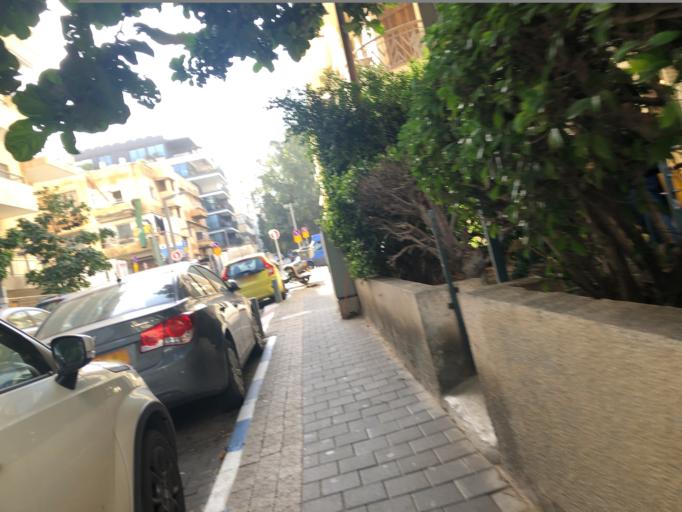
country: IL
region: Tel Aviv
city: Tel Aviv
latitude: 32.0691
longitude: 34.7759
